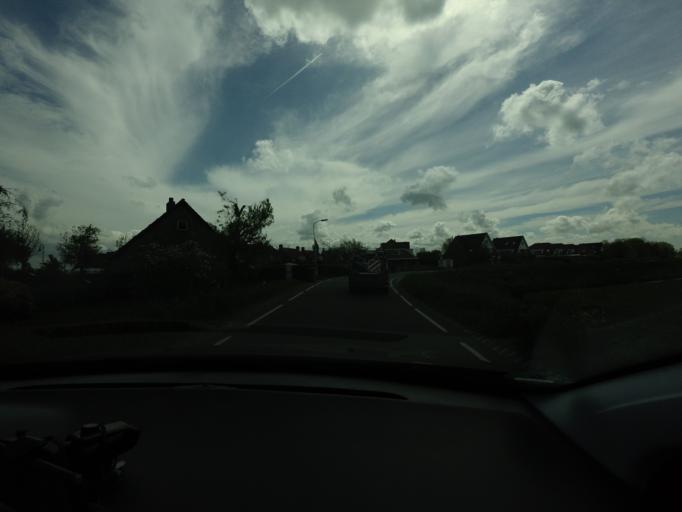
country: NL
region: North Holland
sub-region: Gemeente Heerhugowaard
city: Heerhugowaard
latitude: 52.5796
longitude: 4.8484
